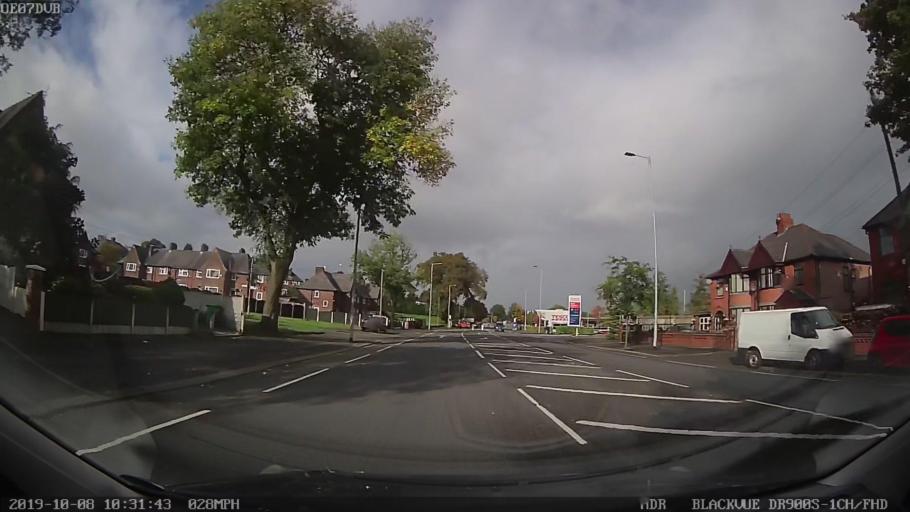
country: GB
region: England
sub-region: Manchester
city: Blackley
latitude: 53.5313
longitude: -2.2044
